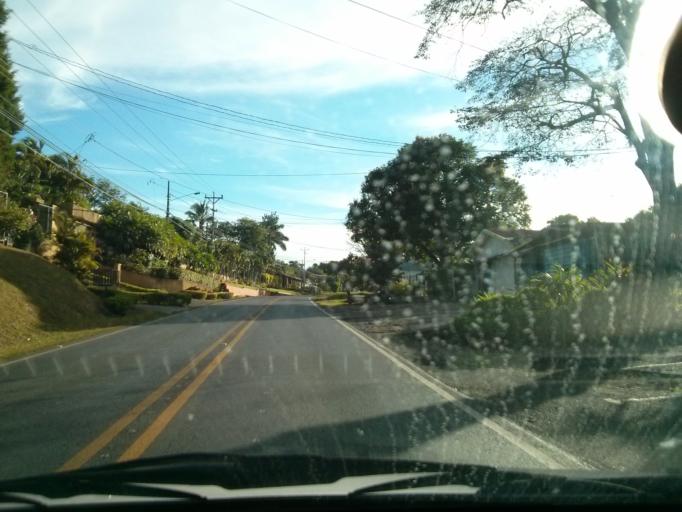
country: CR
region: Alajuela
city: Carrillos
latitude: 10.0113
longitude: -84.2822
